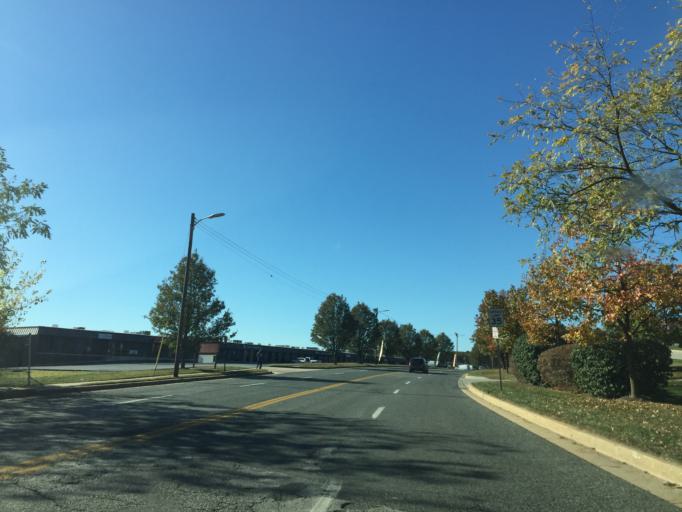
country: US
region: Maryland
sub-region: Baltimore County
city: Lansdowne
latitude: 39.2524
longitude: -76.6642
